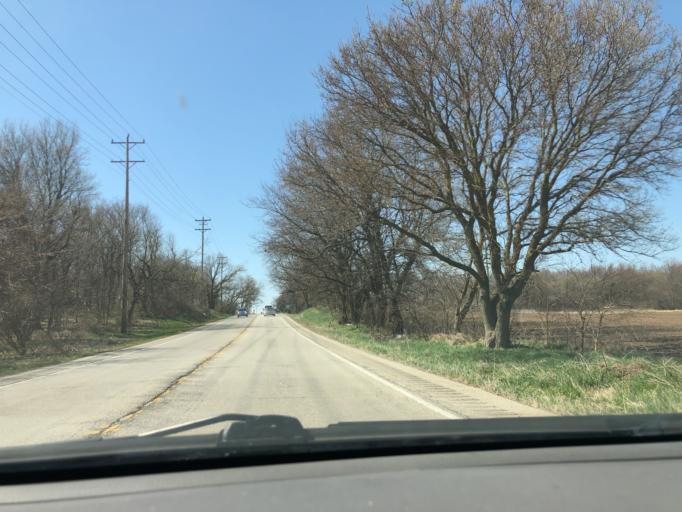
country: US
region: Illinois
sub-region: Kane County
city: Hampshire
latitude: 42.1568
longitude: -88.5217
